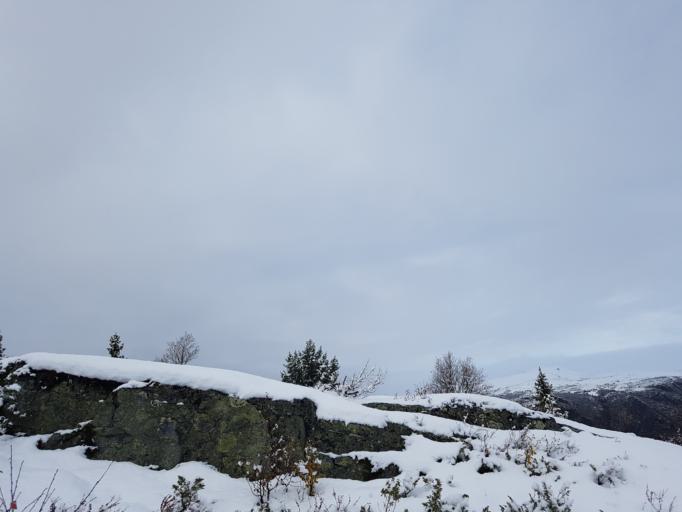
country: NO
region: Oppland
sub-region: Sel
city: Otta
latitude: 61.8049
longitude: 9.6770
